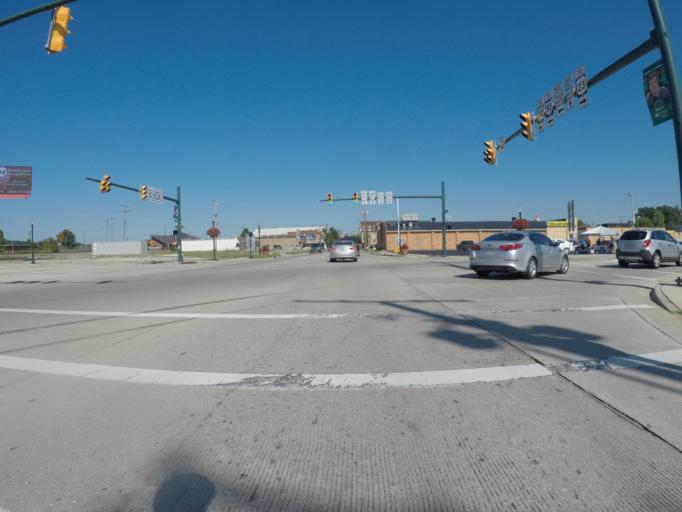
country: US
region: Ohio
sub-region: Lawrence County
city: Ironton
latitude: 38.5308
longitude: -82.6829
